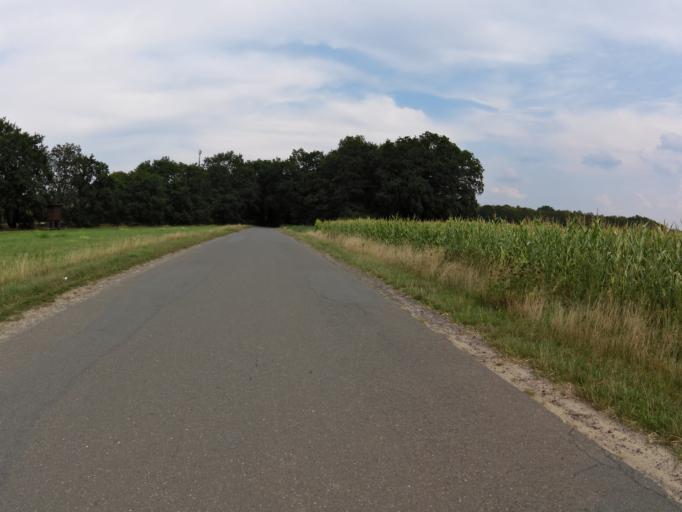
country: DE
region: Lower Saxony
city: Estorf
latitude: 52.6078
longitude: 9.1910
